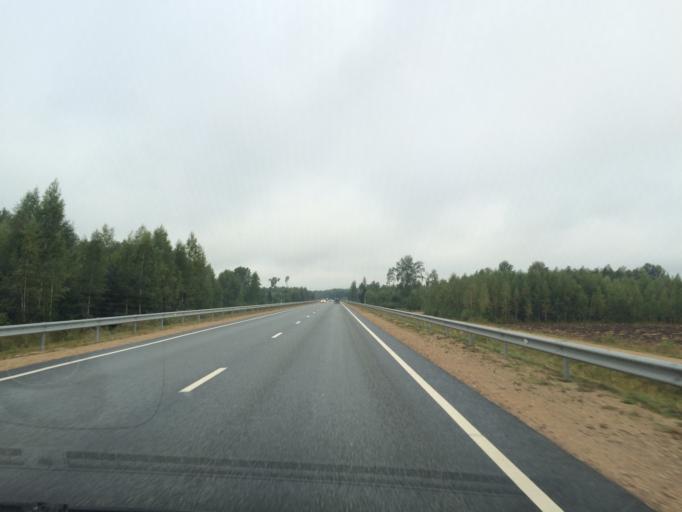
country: LV
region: Lielvarde
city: Lielvarde
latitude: 56.8117
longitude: 24.8607
